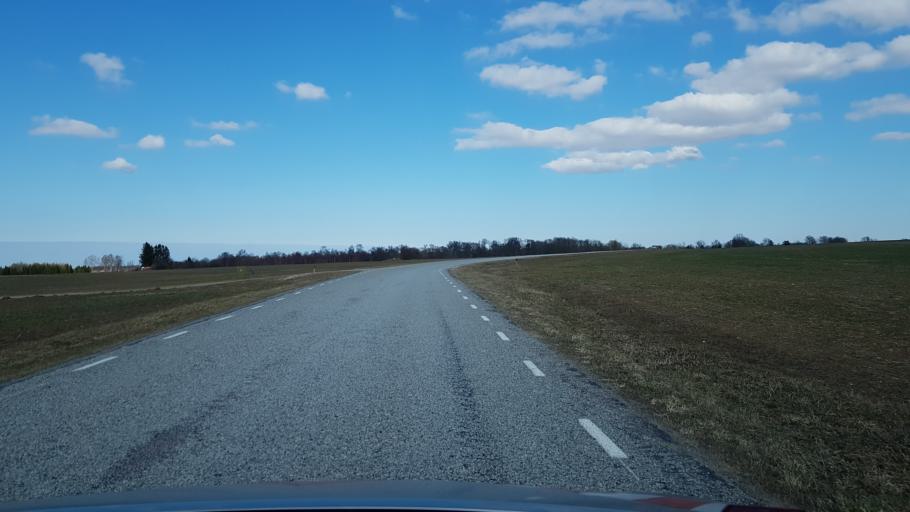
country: EE
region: Laeaene-Virumaa
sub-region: Kadrina vald
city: Kadrina
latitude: 59.3123
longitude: 26.2379
